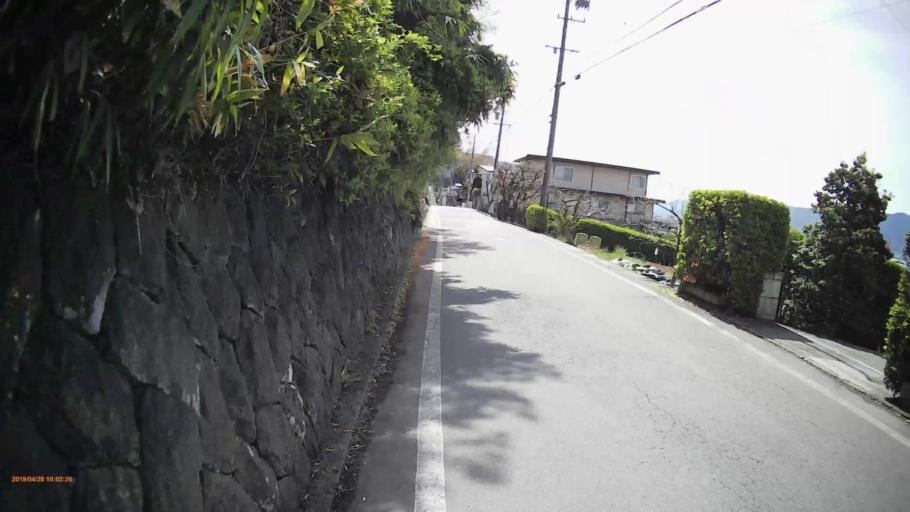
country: JP
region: Nagano
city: Suwa
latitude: 36.0696
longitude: 138.0987
